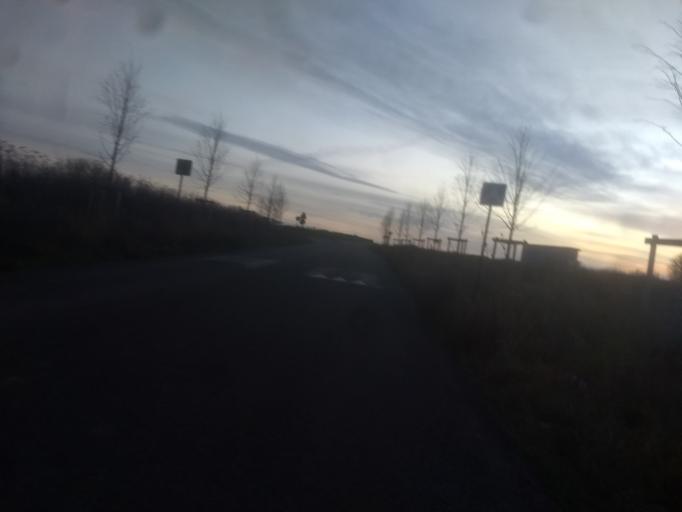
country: FR
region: Nord-Pas-de-Calais
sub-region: Departement du Pas-de-Calais
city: Achicourt
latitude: 50.2795
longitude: 2.7426
